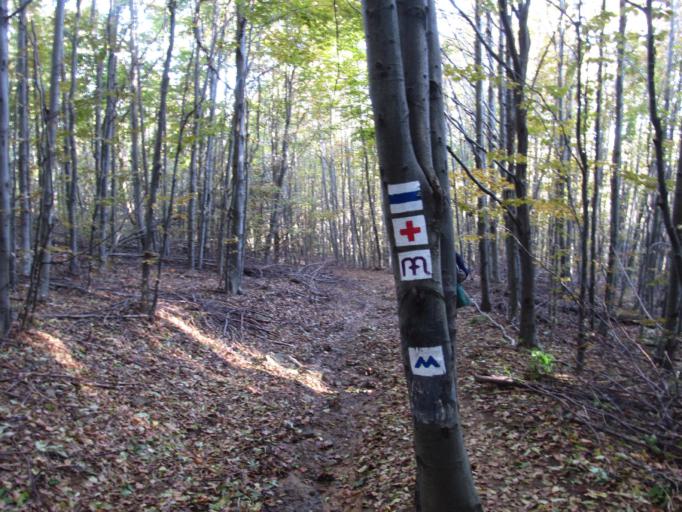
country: HU
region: Heves
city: Paradsasvar
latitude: 47.9180
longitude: 19.9307
